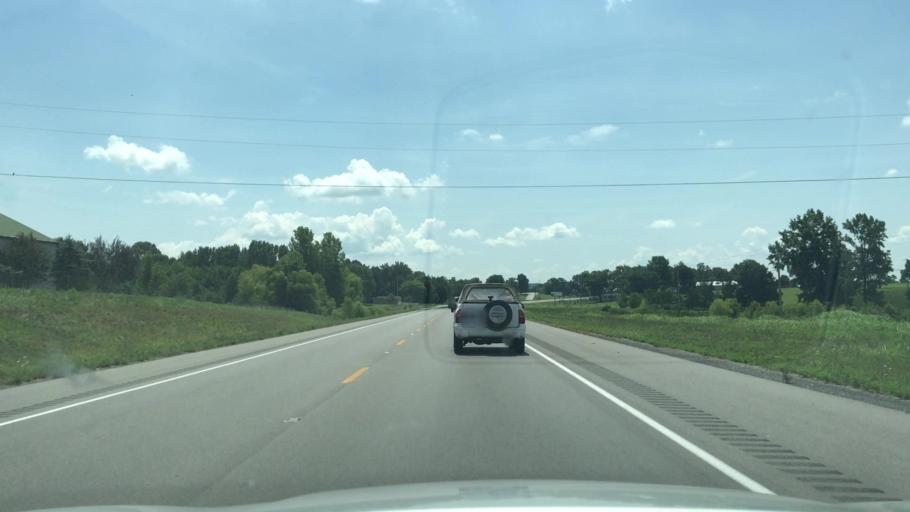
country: US
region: Tennessee
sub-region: Pickett County
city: Byrdstown
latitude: 36.6295
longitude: -85.0929
